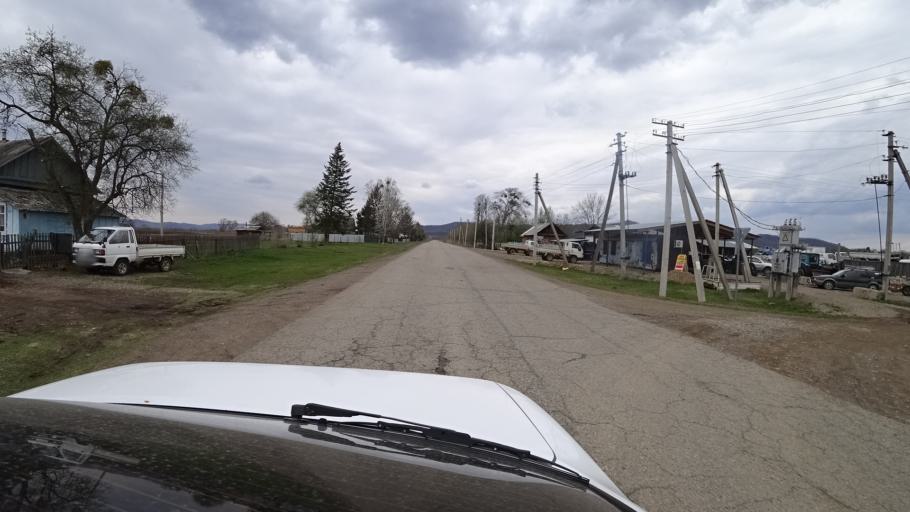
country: RU
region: Primorskiy
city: Novopokrovka
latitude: 45.5509
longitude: 134.3630
